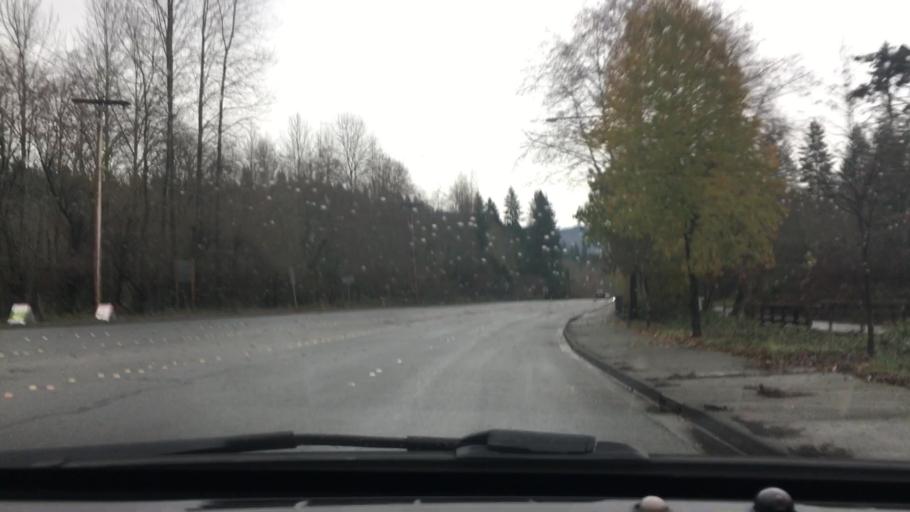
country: US
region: Washington
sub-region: King County
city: City of Sammamish
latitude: 47.5669
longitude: -122.0539
